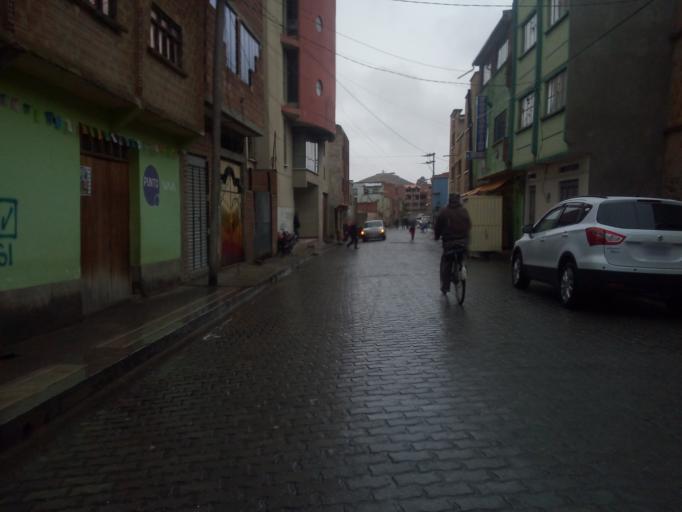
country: BO
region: La Paz
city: Achacachi
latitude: -16.0433
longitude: -68.6892
